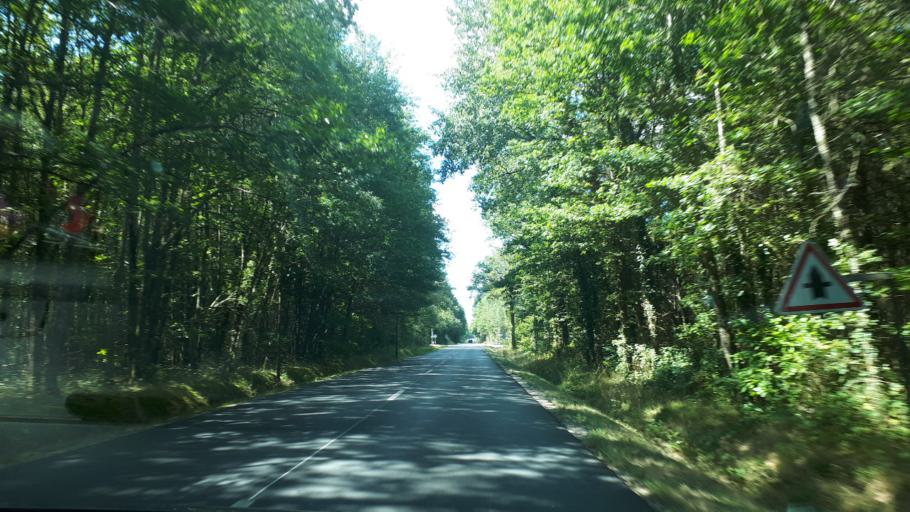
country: FR
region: Centre
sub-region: Departement du Loir-et-Cher
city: Chaumont-sur-Tharonne
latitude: 47.5733
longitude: 1.9211
